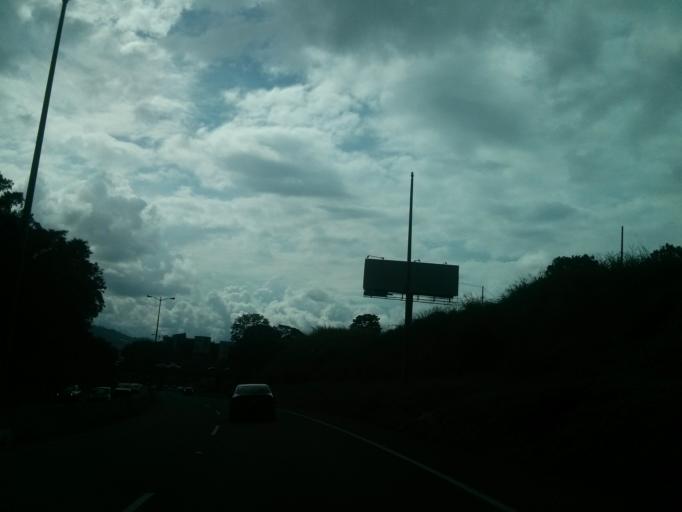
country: CR
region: San Jose
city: San Rafael
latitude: 9.9364
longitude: -84.1144
